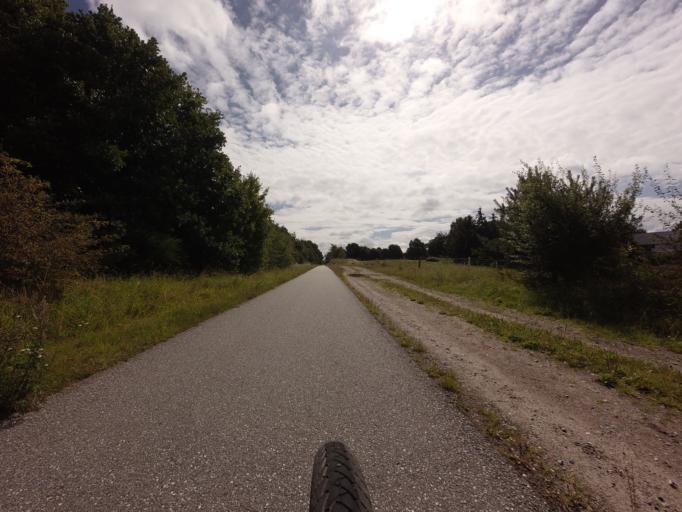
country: DK
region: Central Jutland
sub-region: Norddjurs Kommune
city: Allingabro
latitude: 56.4564
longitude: 10.3470
